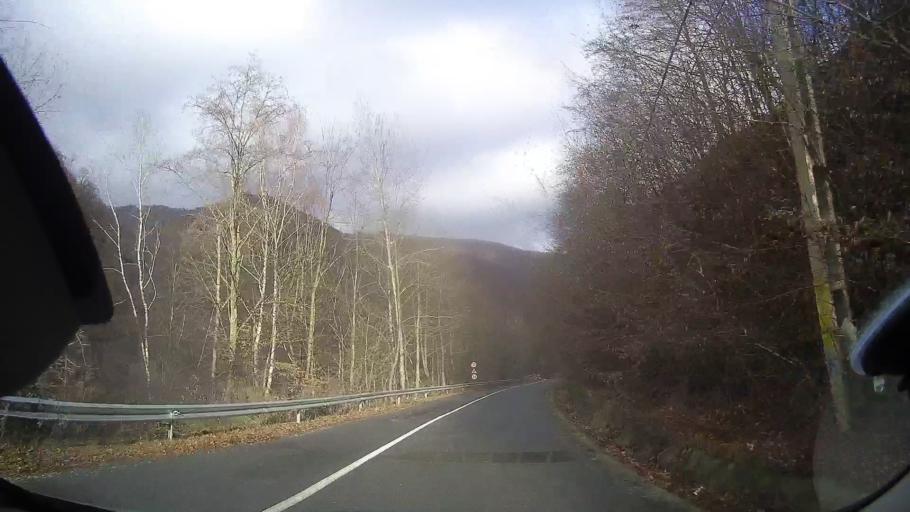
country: RO
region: Cluj
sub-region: Comuna Valea Ierii
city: Valea Ierii
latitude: 46.6877
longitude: 23.3069
